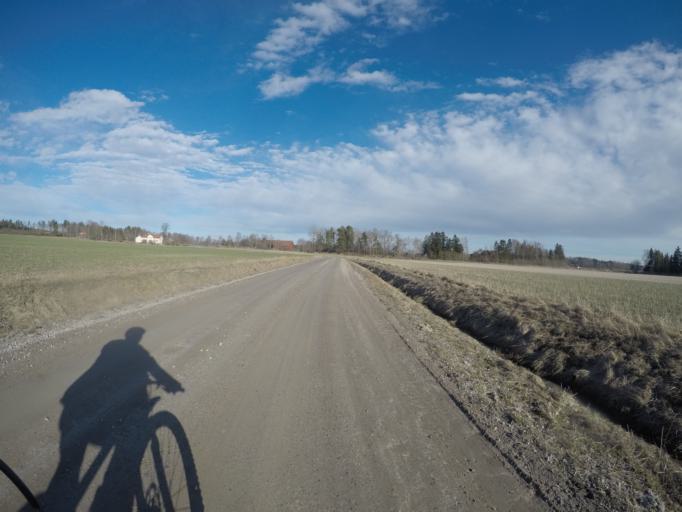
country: SE
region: Vaestmanland
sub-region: Kungsors Kommun
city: Kungsoer
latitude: 59.4176
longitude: 16.2016
